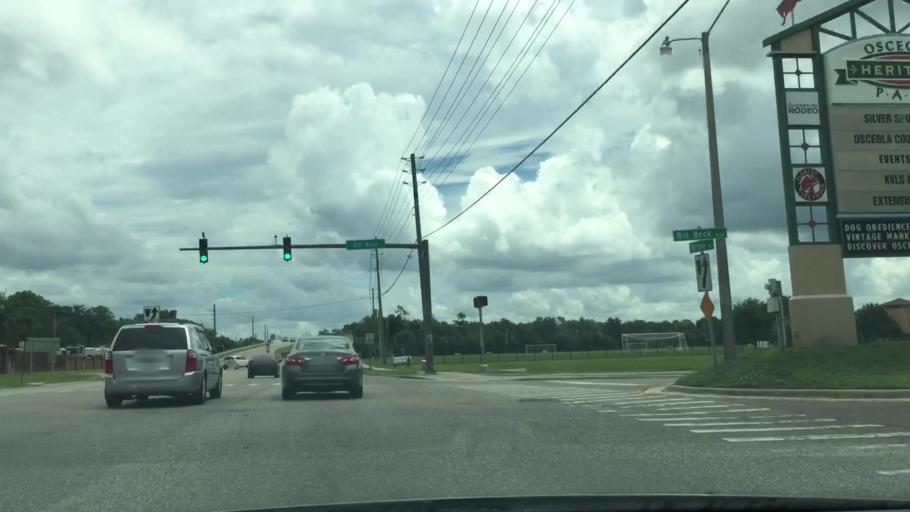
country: US
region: Florida
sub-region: Osceola County
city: Buenaventura Lakes
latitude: 28.3041
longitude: -81.3657
